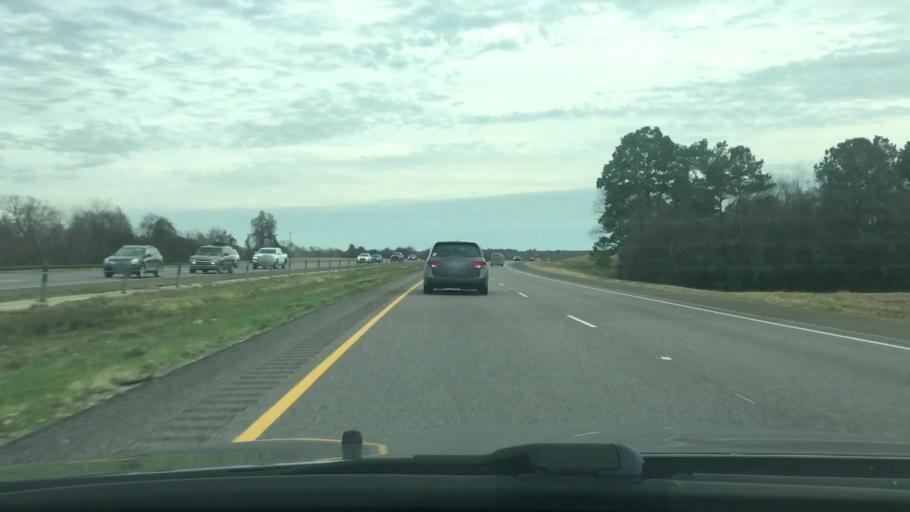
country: US
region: Texas
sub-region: Madison County
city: Madisonville
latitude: 30.9105
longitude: -95.7918
